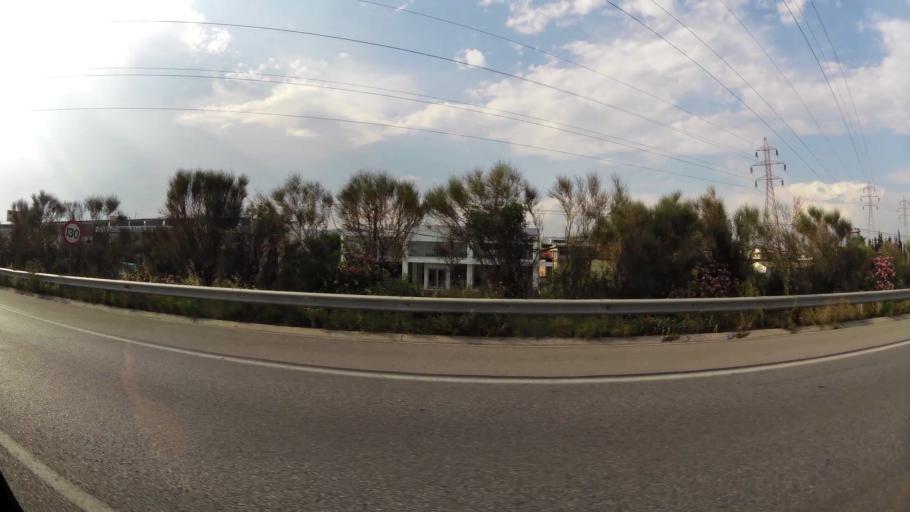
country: GR
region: Central Macedonia
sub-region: Nomos Thessalonikis
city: Efkarpia
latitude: 40.6953
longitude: 22.9303
